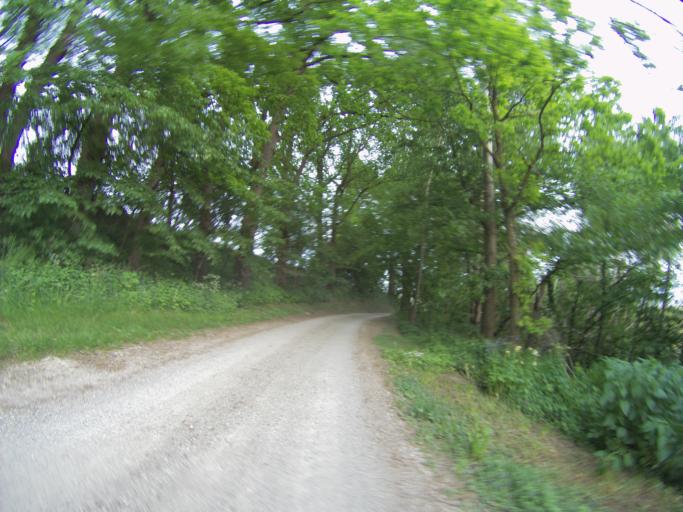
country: DE
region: Bavaria
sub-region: Upper Bavaria
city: Freising
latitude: 48.4180
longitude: 11.7669
